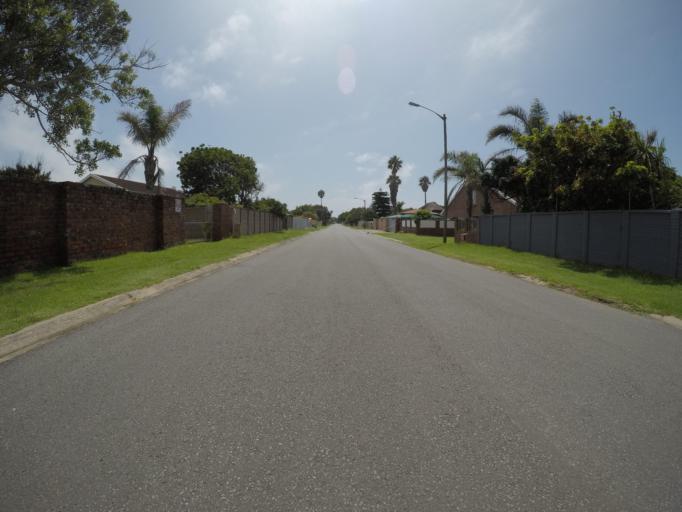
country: ZA
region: Eastern Cape
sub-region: Buffalo City Metropolitan Municipality
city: East London
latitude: -32.9485
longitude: 28.0161
